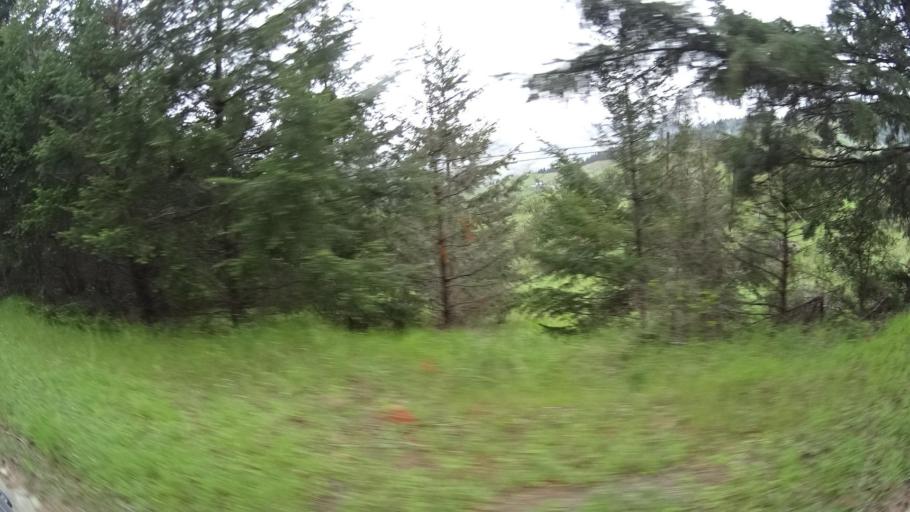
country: US
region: California
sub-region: Humboldt County
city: Redway
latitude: 40.1078
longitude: -123.7480
